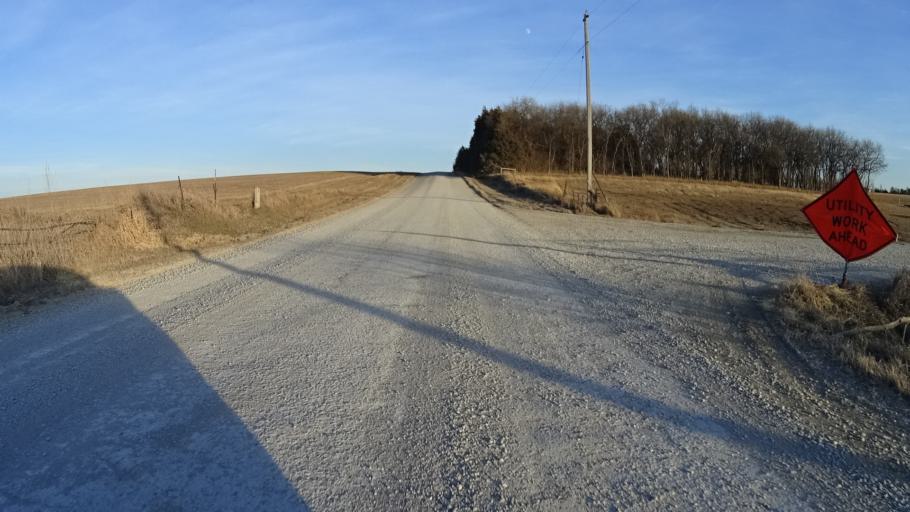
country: US
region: Nebraska
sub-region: Sarpy County
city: Springfield
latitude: 41.1326
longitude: -96.1160
